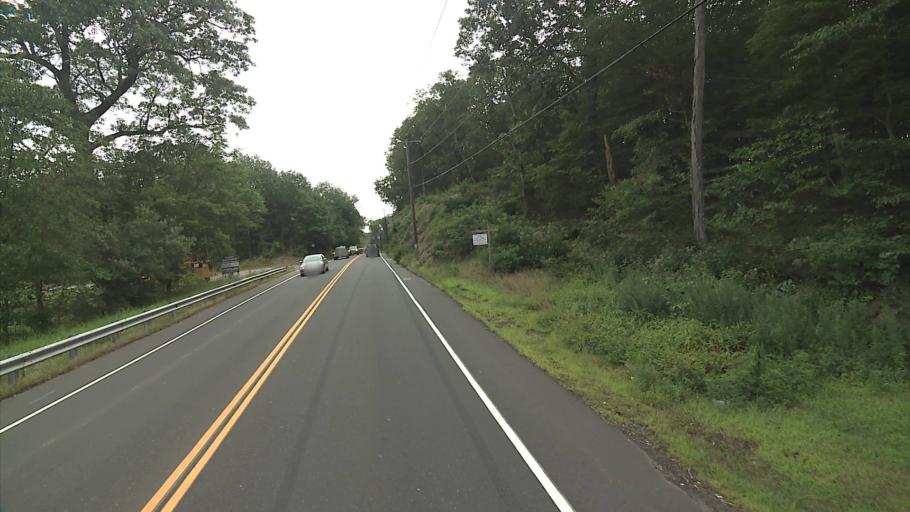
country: US
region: Connecticut
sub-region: New Haven County
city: Branford
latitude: 41.2902
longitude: -72.8043
